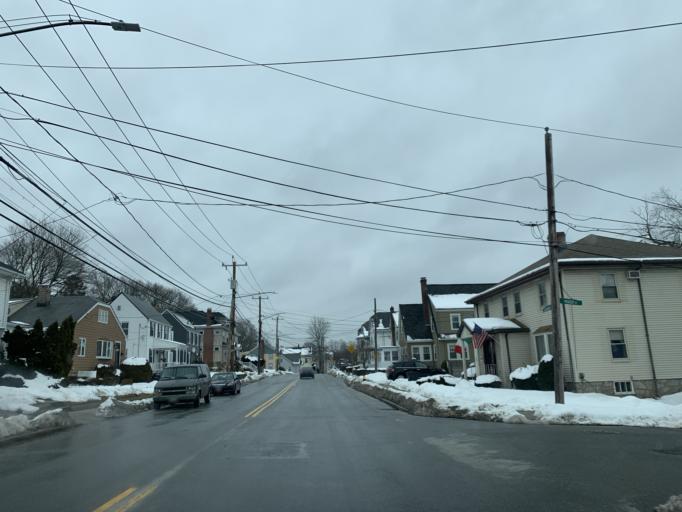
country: US
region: Massachusetts
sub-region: Norfolk County
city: Dedham
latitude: 42.2849
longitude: -71.1627
